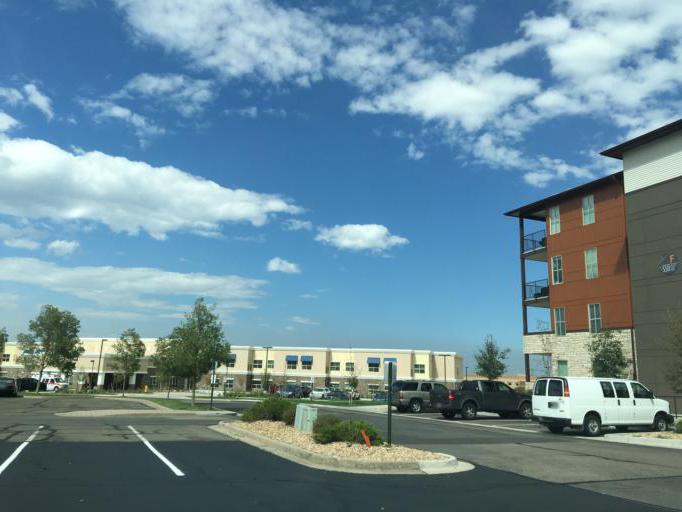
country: US
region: Colorado
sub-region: Jefferson County
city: West Pleasant View
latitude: 39.7260
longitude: -105.2050
